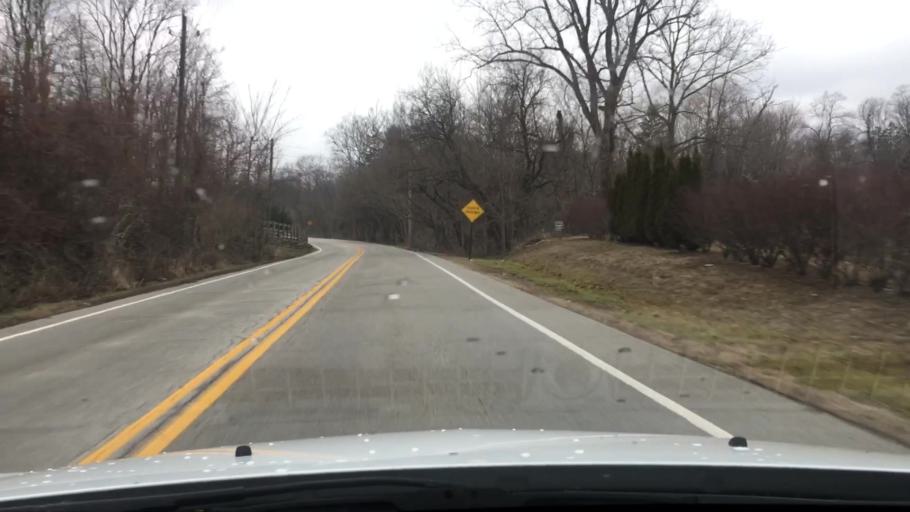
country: US
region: Indiana
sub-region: Boone County
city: Zionsville
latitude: 39.8813
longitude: -86.2873
